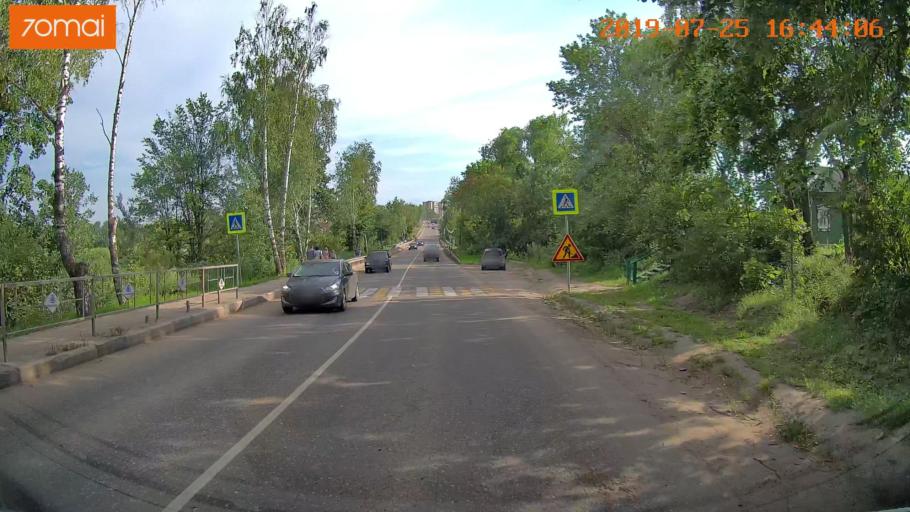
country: RU
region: Ivanovo
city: Privolzhsk
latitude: 57.3781
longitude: 41.2798
